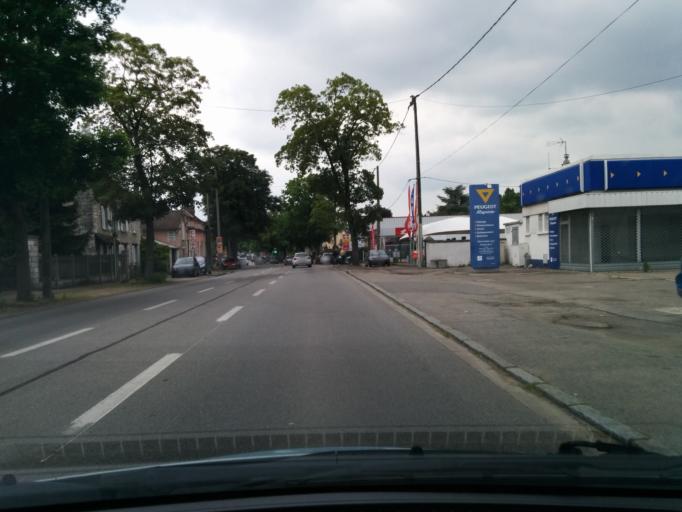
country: FR
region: Haute-Normandie
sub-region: Departement de l'Eure
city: Vernon
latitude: 49.0856
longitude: 1.4982
